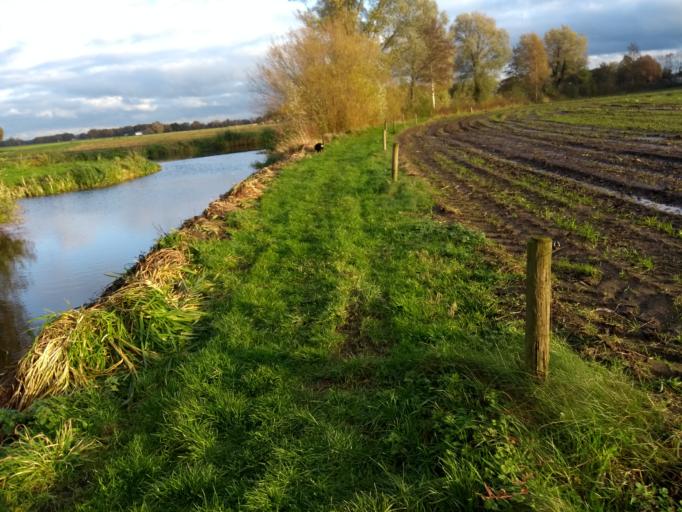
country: NL
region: Overijssel
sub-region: Gemeente Borne
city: Borne
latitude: 52.3407
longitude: 6.7316
